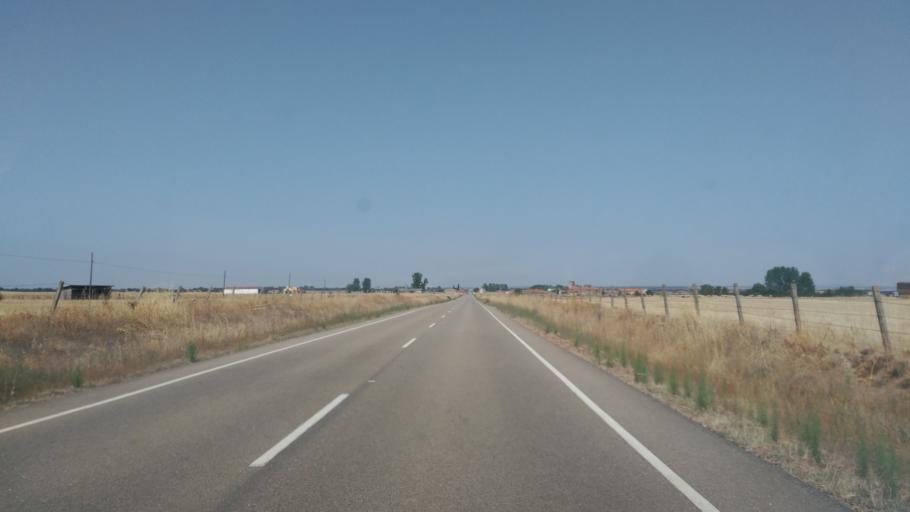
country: ES
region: Castille and Leon
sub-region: Provincia de Salamanca
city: La Fuente de San Esteban
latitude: 40.7707
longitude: -6.2235
